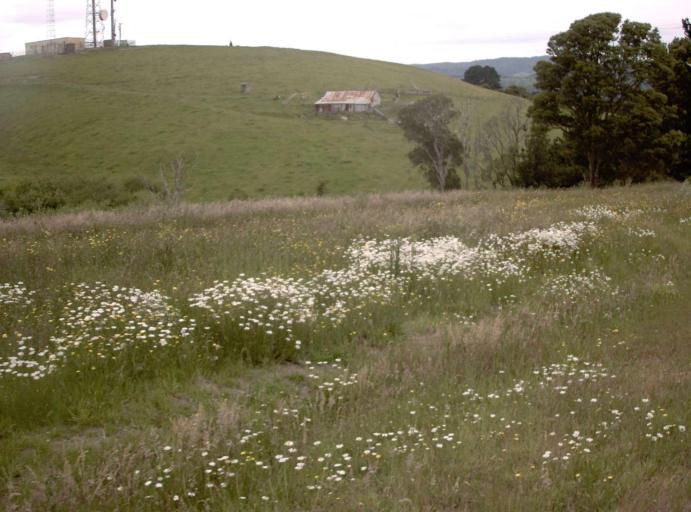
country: AU
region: Victoria
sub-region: Latrobe
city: Morwell
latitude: -38.6211
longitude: 146.1721
